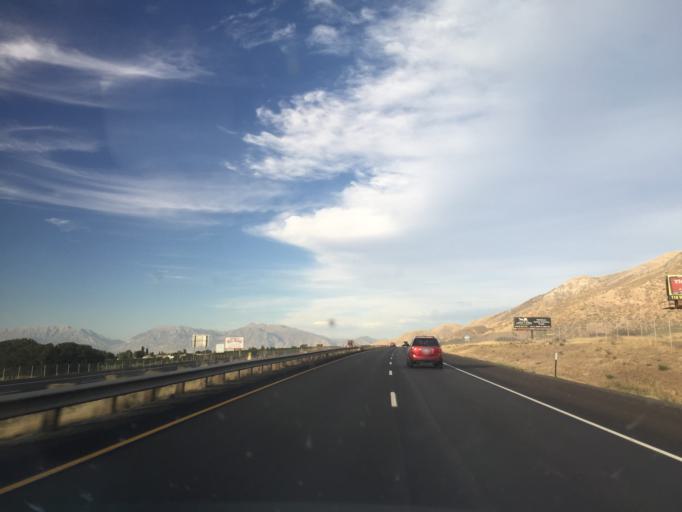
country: US
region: Utah
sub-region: Utah County
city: Santaquin
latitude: 39.9586
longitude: -111.7949
